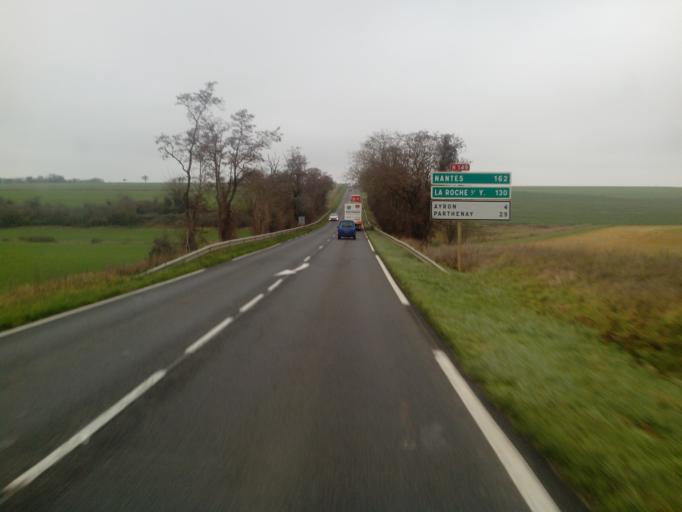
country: FR
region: Poitou-Charentes
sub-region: Departement de la Vienne
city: Ayron
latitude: 46.6533
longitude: 0.1205
